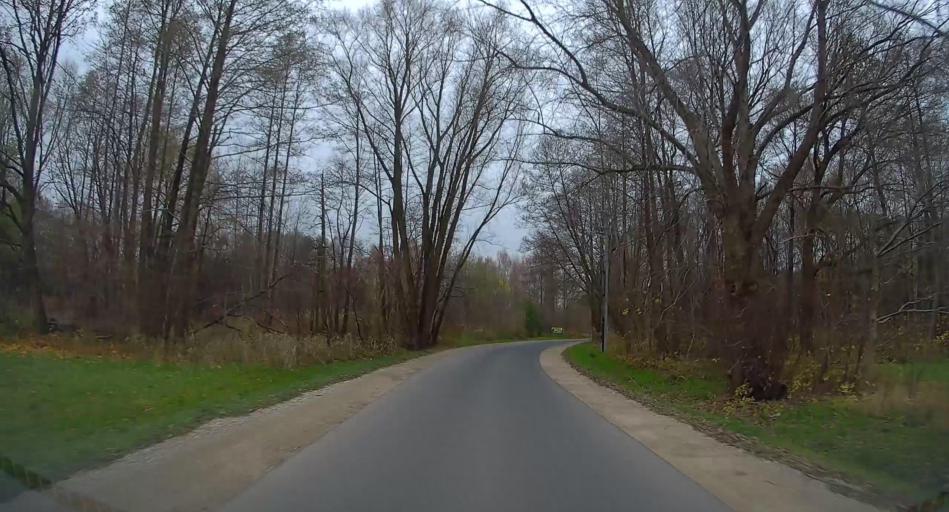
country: PL
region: Lodz Voivodeship
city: Zabia Wola
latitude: 52.0180
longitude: 20.6559
